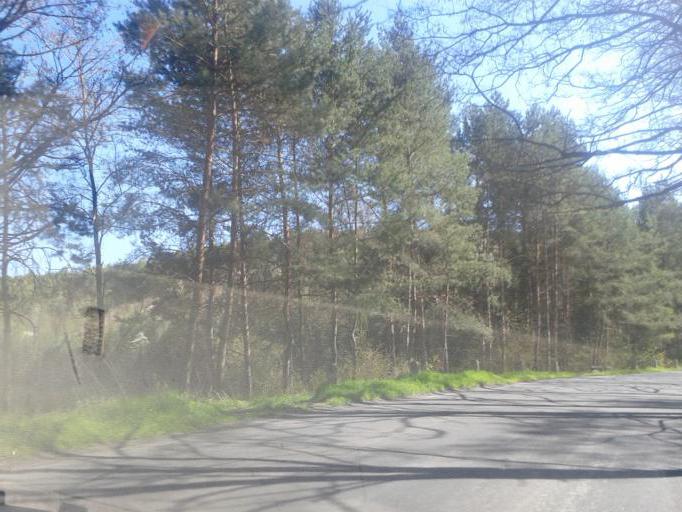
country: CZ
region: Central Bohemia
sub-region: Okres Beroun
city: Kraluv Dvur
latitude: 49.9340
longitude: 14.0444
